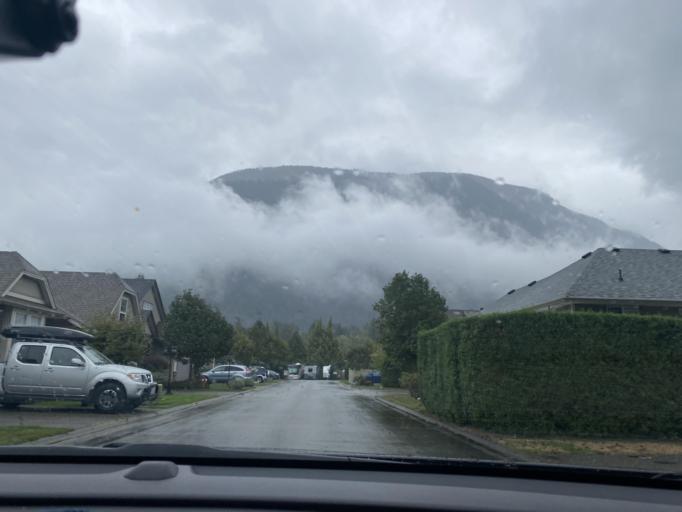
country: CA
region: British Columbia
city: Agassiz
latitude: 49.2998
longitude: -121.7829
